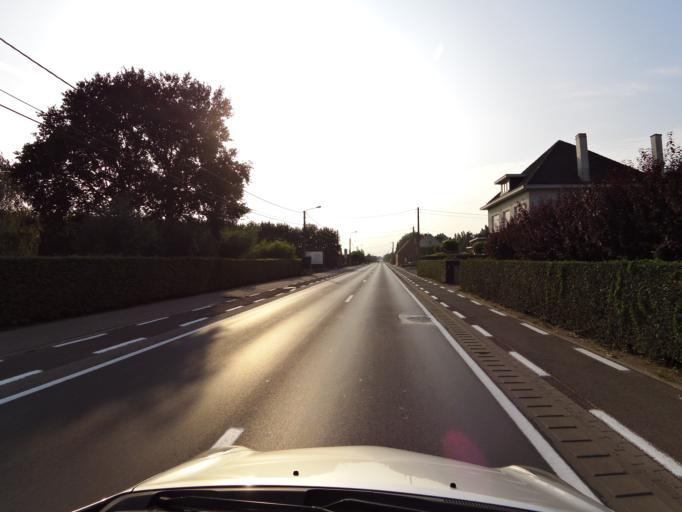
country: BE
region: Flanders
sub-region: Provincie West-Vlaanderen
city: Ardooie
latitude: 51.0013
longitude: 3.2034
